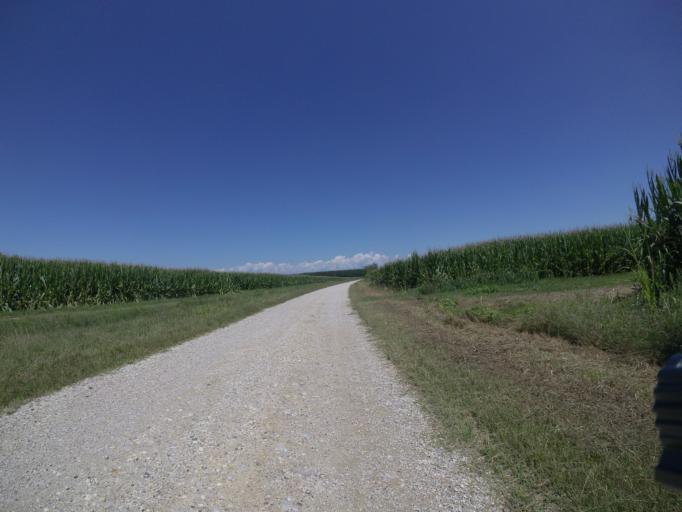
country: IT
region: Friuli Venezia Giulia
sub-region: Provincia di Udine
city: Talmassons
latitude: 45.8934
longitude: 13.0960
